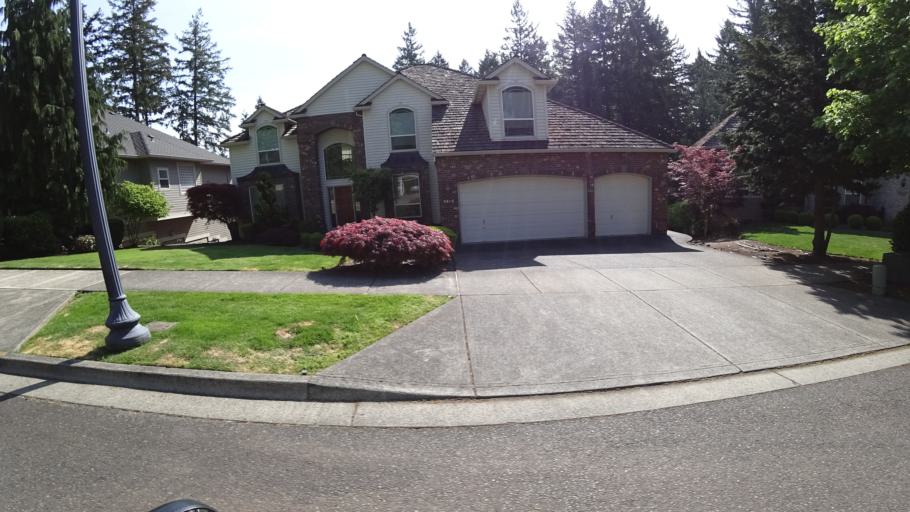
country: US
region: Oregon
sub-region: Washington County
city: Aloha
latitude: 45.4491
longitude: -122.8474
